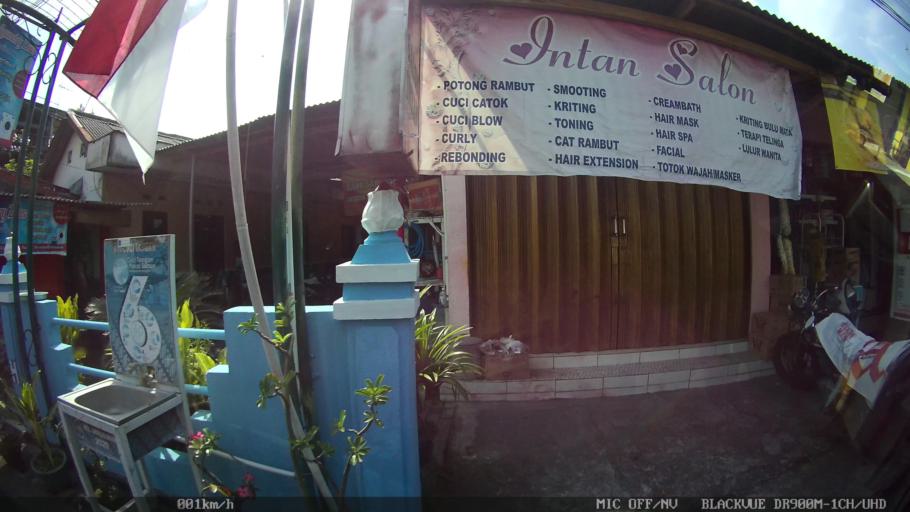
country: ID
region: Daerah Istimewa Yogyakarta
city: Yogyakarta
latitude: -7.8055
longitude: 110.3753
